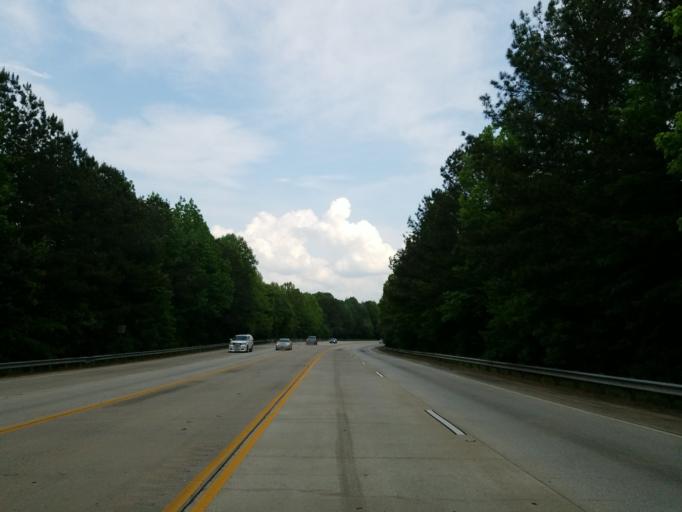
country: US
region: Georgia
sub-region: Cobb County
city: Powder Springs
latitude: 33.8309
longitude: -84.6719
